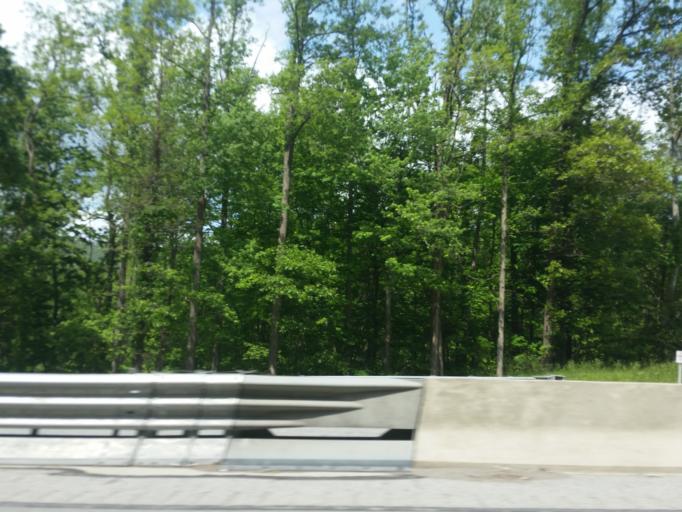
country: US
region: West Virginia
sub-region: Fayette County
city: Oak Hill
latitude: 37.9890
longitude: -81.3132
